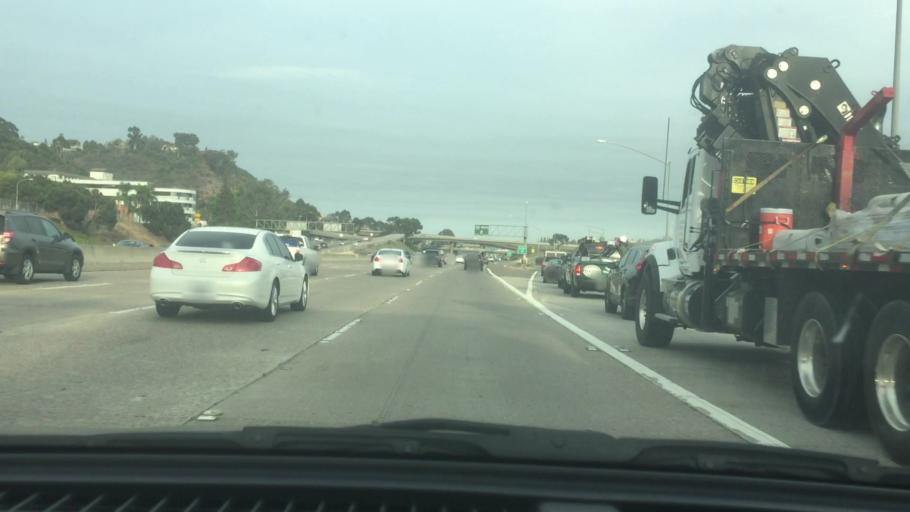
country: US
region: California
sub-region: San Diego County
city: Lemon Grove
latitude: 32.7789
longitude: -117.1042
